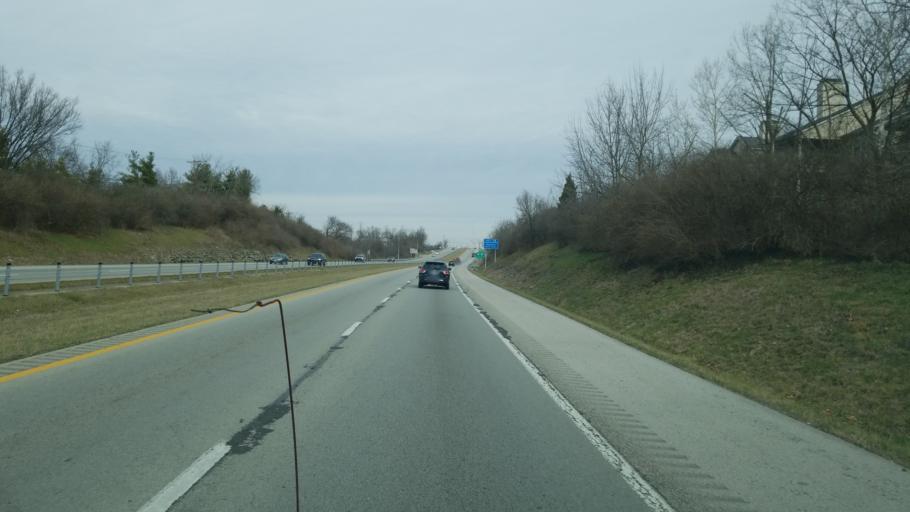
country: US
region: Kentucky
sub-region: Fayette County
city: Lexington
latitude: 38.0047
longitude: -84.4611
